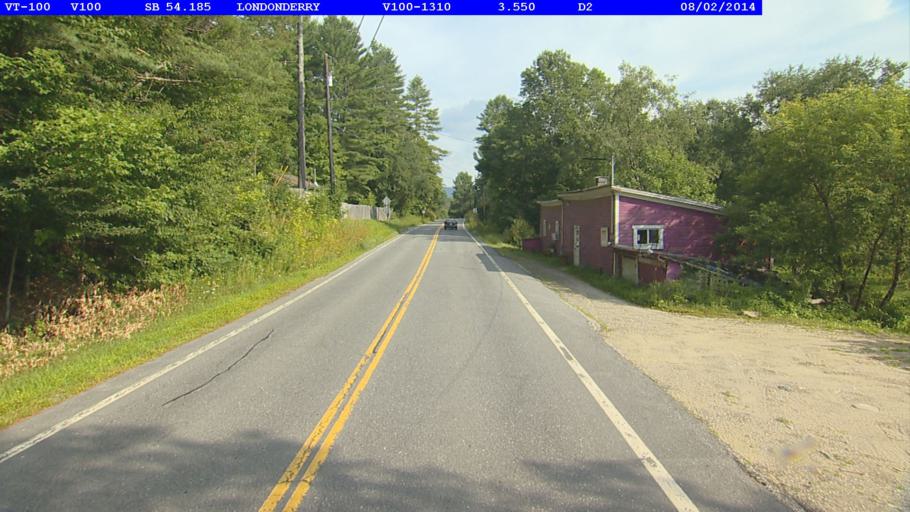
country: US
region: Vermont
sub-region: Windsor County
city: Chester
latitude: 43.1990
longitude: -72.8207
